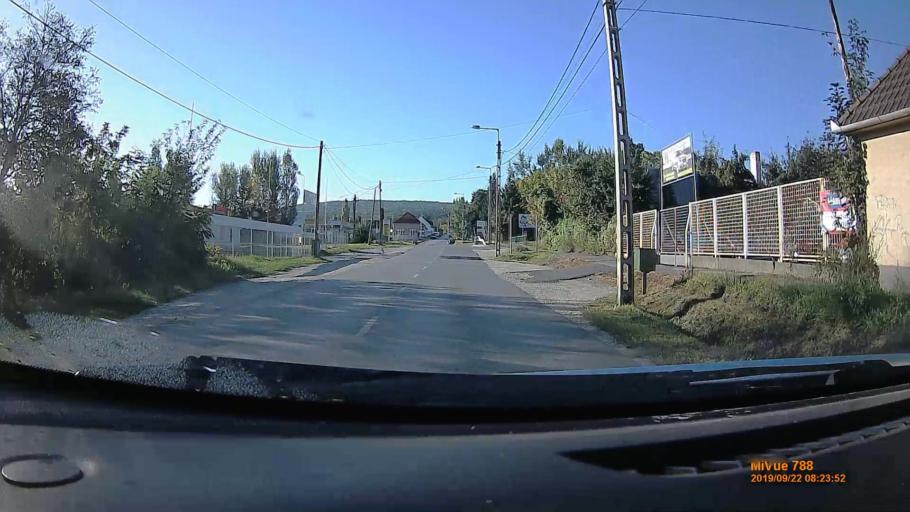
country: HU
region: Borsod-Abauj-Zemplen
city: Miskolc
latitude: 48.0946
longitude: 20.7111
